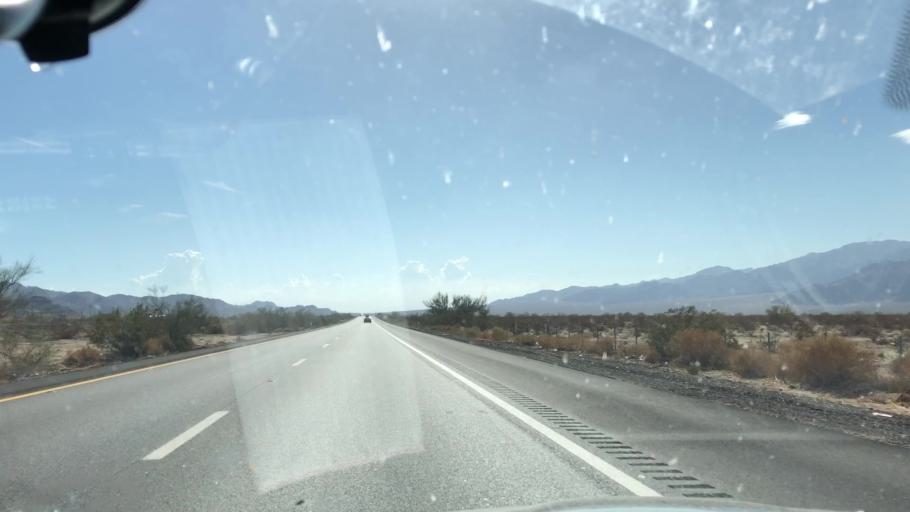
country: US
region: California
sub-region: Imperial County
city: Niland
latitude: 33.6726
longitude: -115.5971
